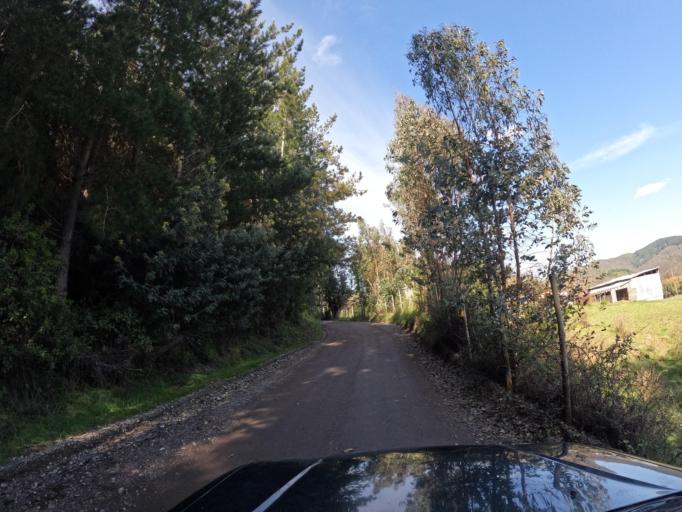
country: CL
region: Biobio
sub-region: Provincia de Concepcion
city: Chiguayante
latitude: -37.0615
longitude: -72.8925
